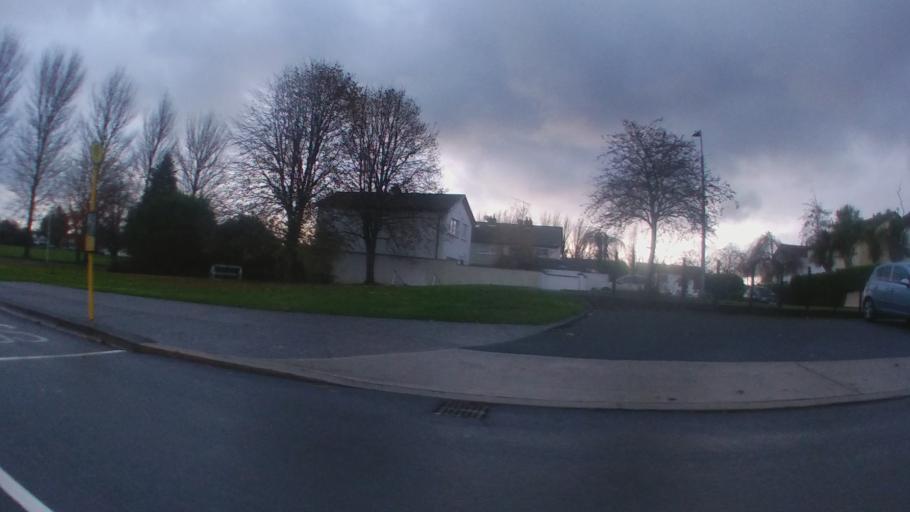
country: IE
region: Leinster
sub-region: Wicklow
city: Kilcoole
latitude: 53.1063
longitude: -6.0631
